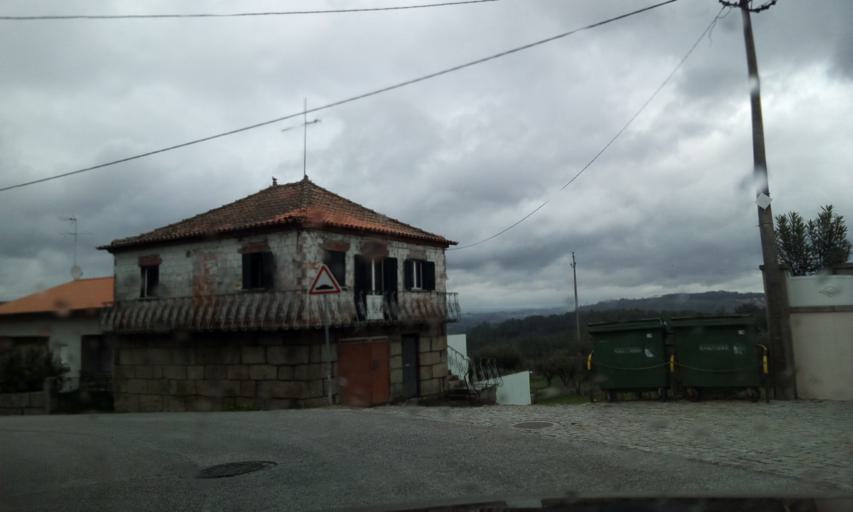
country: PT
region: Viseu
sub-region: Nelas
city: Nelas
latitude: 40.6022
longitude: -7.8450
